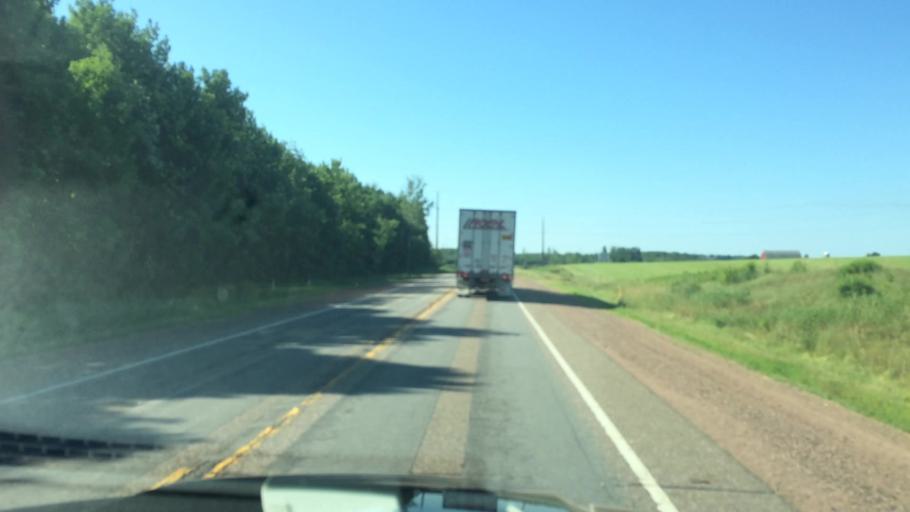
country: US
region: Wisconsin
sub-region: Marathon County
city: Athens
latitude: 44.9380
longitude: -90.0791
